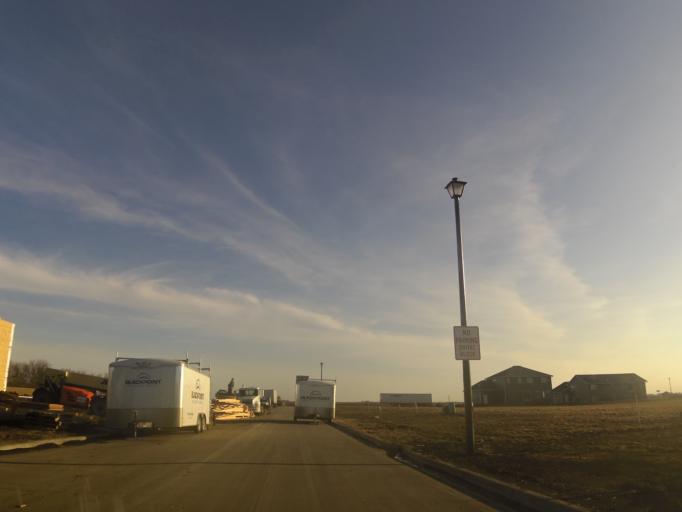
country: US
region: North Dakota
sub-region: Grand Forks County
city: Grand Forks
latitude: 47.8637
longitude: -97.0250
